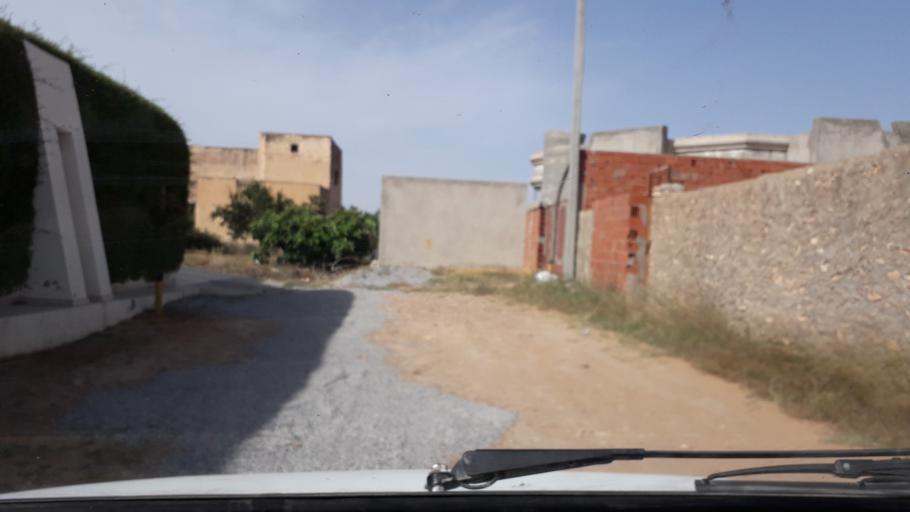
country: TN
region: Safaqis
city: Al Qarmadah
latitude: 34.8068
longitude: 10.7698
